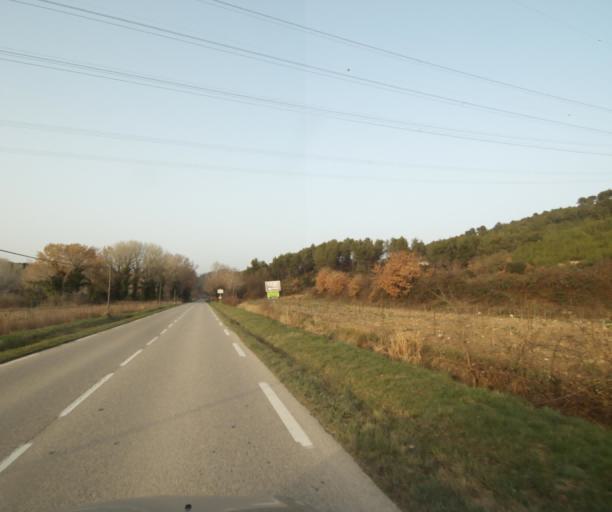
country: FR
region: Provence-Alpes-Cote d'Azur
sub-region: Departement des Bouches-du-Rhone
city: Rognes
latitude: 43.6995
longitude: 5.3474
